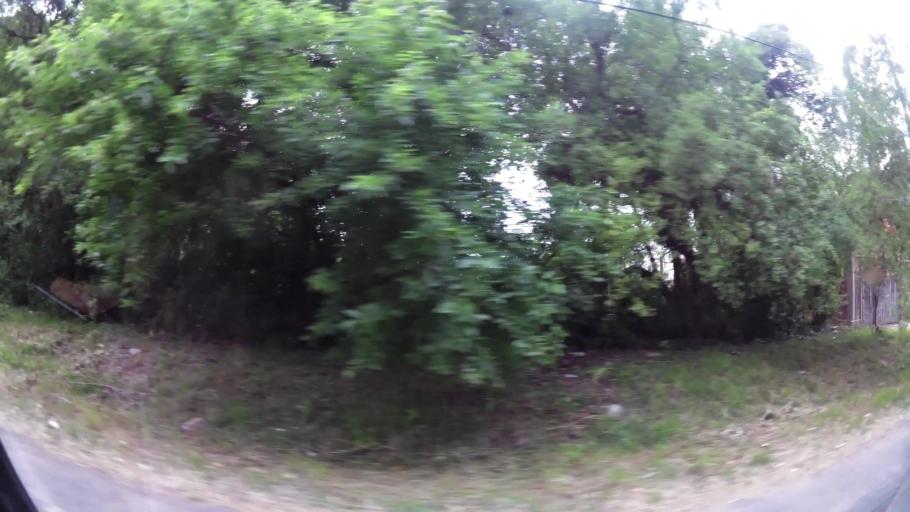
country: AR
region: Buenos Aires
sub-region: Partido de La Plata
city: La Plata
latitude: -34.9267
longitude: -57.9943
